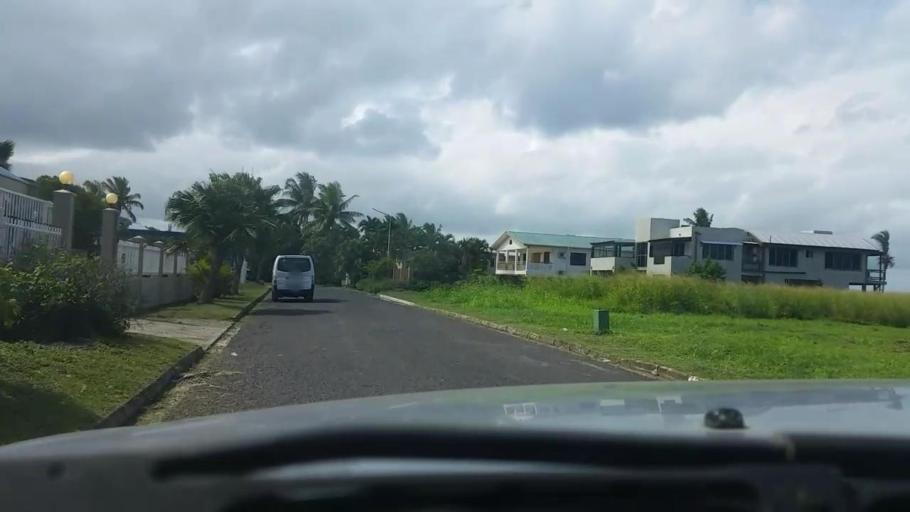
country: FJ
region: Central
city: Suva
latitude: -18.1329
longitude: 178.4657
